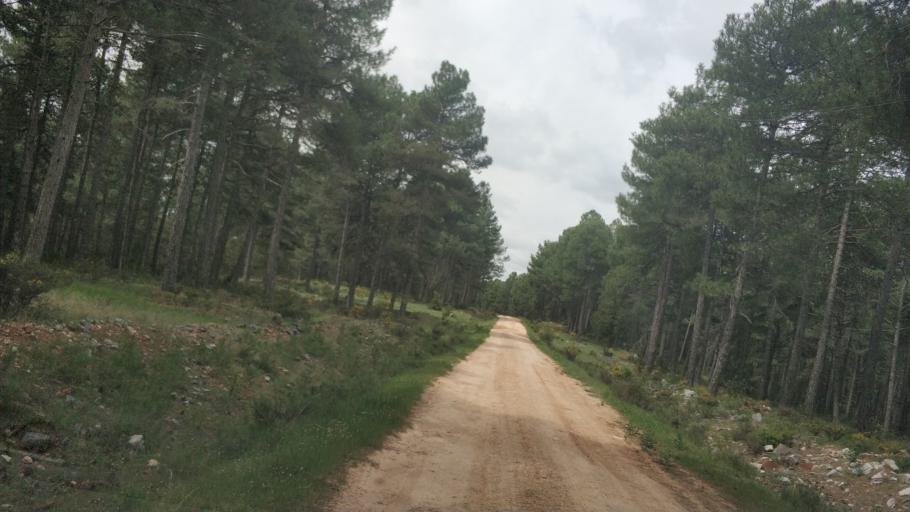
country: ES
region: Castille and Leon
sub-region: Provincia de Soria
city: Casarejos
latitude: 41.7691
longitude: -3.0489
